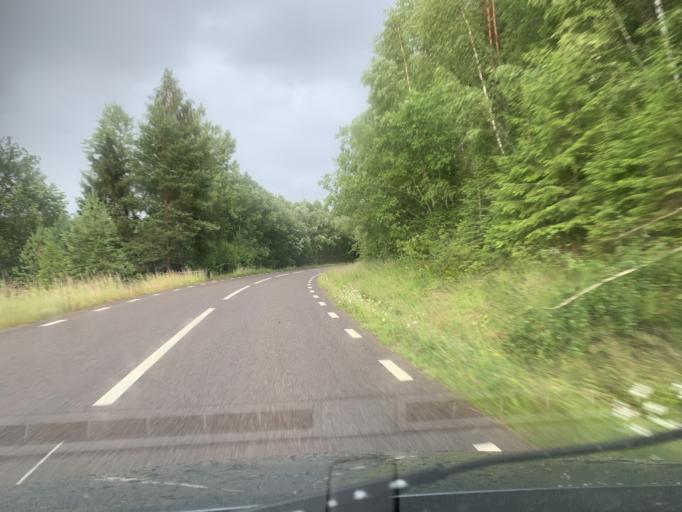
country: SE
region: Kalmar
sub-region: Vasterviks Kommun
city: Overum
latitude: 58.0202
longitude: 16.1405
